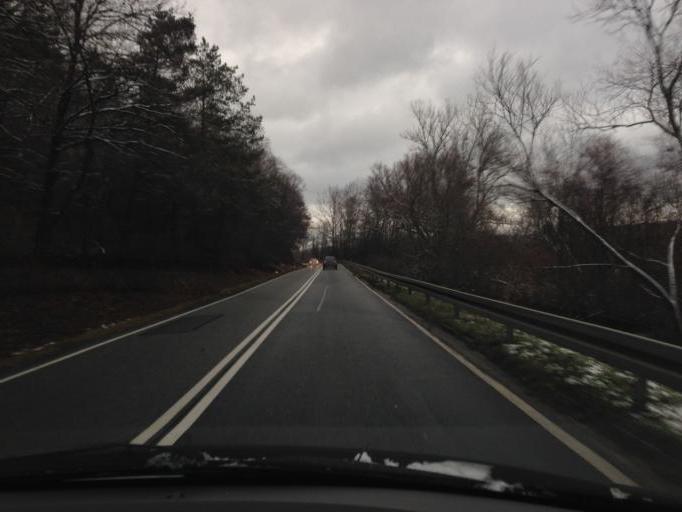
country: PL
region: Lesser Poland Voivodeship
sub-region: Powiat tarnowski
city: Zakliczyn
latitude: 49.8679
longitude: 20.7862
